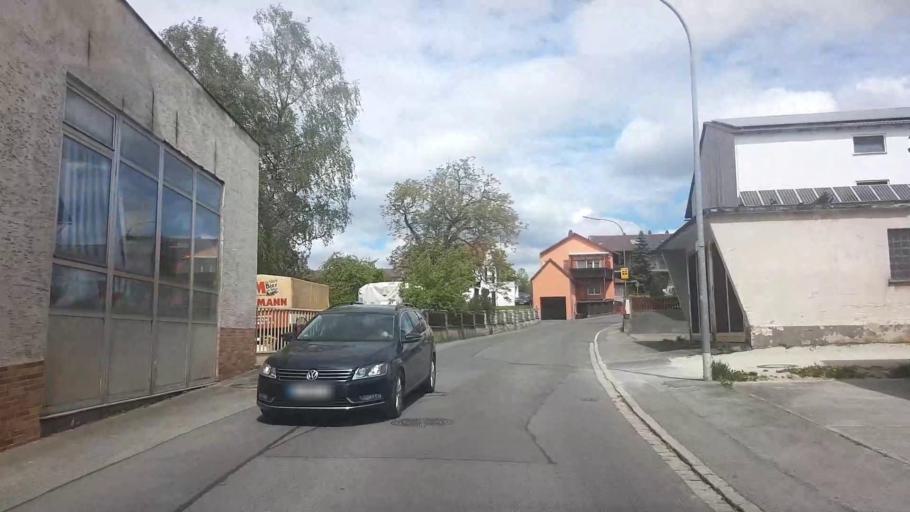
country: DE
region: Bavaria
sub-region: Upper Franconia
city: Untersiemau
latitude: 50.1946
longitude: 10.9735
